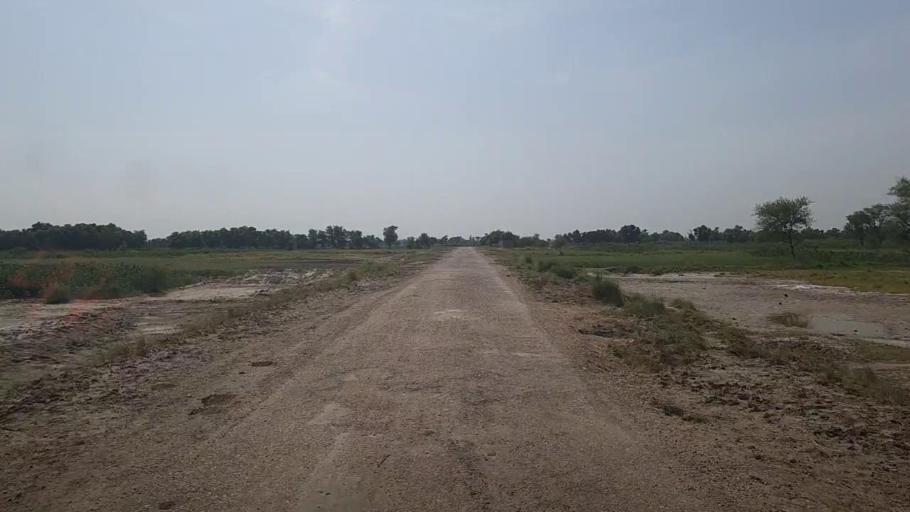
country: PK
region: Sindh
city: Ubauro
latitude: 28.1379
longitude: 69.8216
